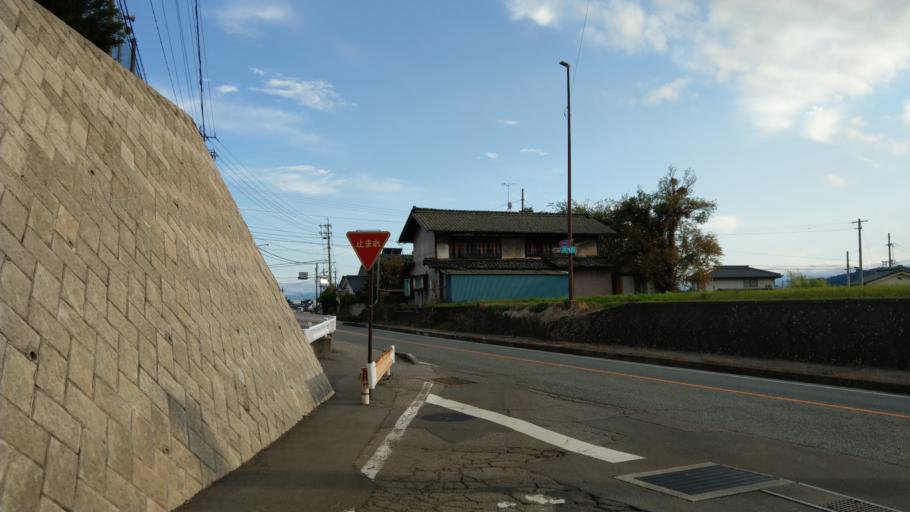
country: JP
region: Nagano
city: Komoro
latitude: 36.3334
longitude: 138.4202
